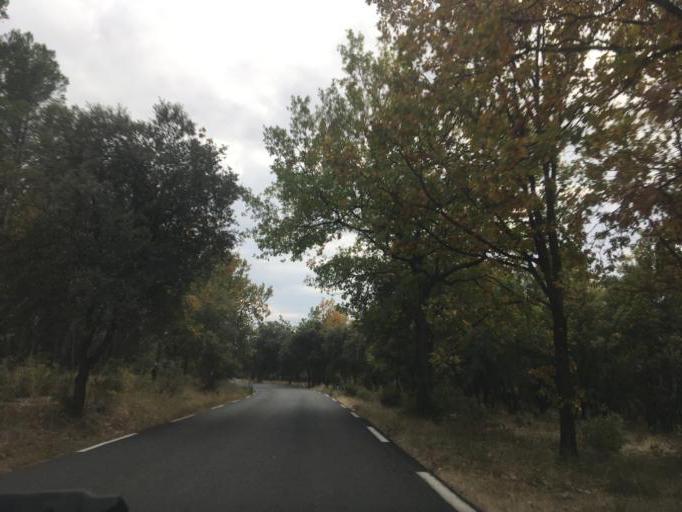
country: FR
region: Provence-Alpes-Cote d'Azur
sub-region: Departement du Var
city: Villecroze
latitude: 43.5582
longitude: 6.3292
